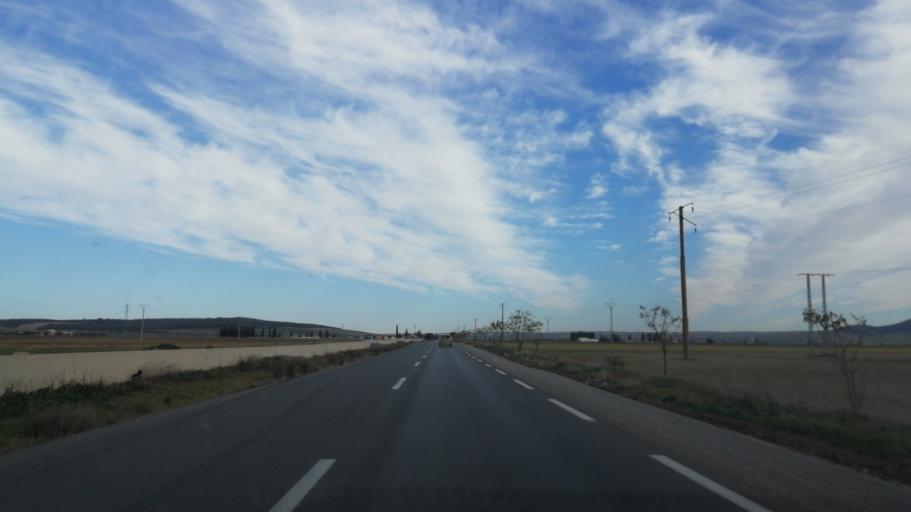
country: DZ
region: Sidi Bel Abbes
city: Sidi Bel Abbes
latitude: 35.1791
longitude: -0.4736
